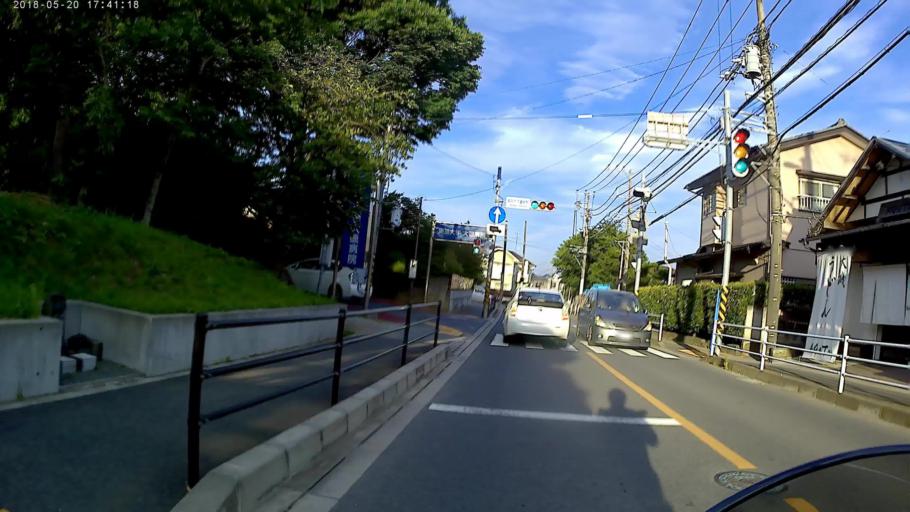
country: JP
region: Kanagawa
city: Ninomiya
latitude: 35.3097
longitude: 139.2743
